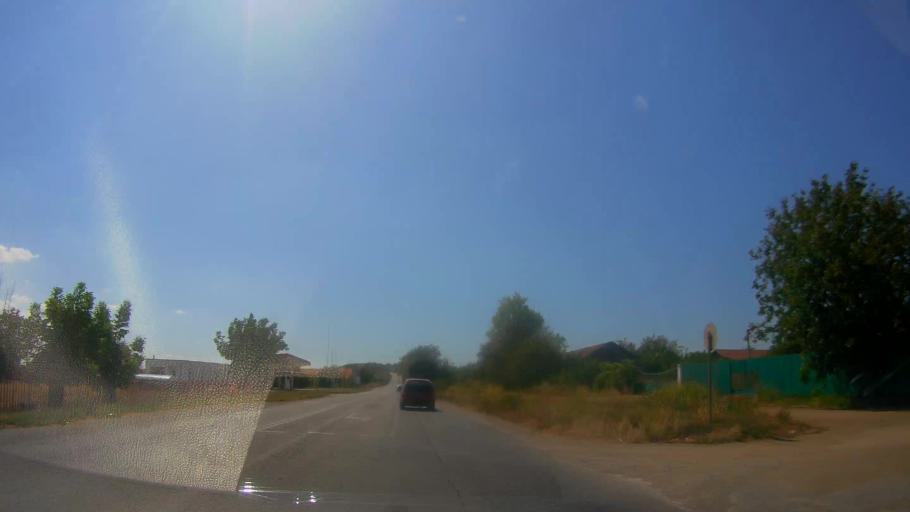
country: BG
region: Veliko Turnovo
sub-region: Obshtina Gorna Oryakhovitsa
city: Purvomaytsi
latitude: 43.2618
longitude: 25.6428
